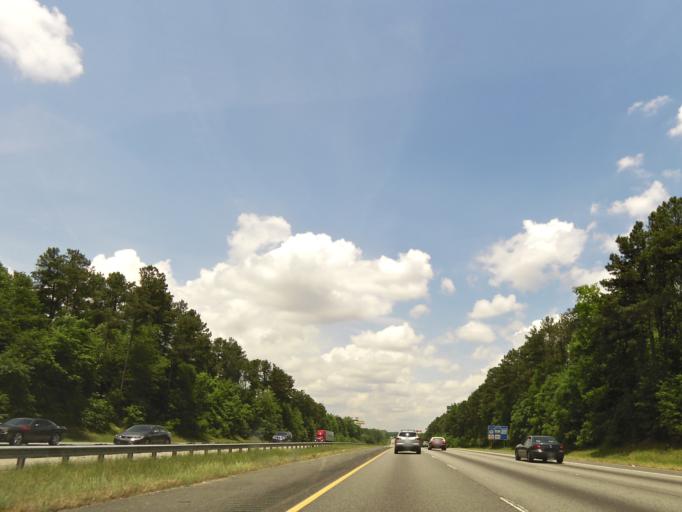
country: US
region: Georgia
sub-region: Henry County
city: Locust Grove
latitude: 33.3352
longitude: -84.1225
